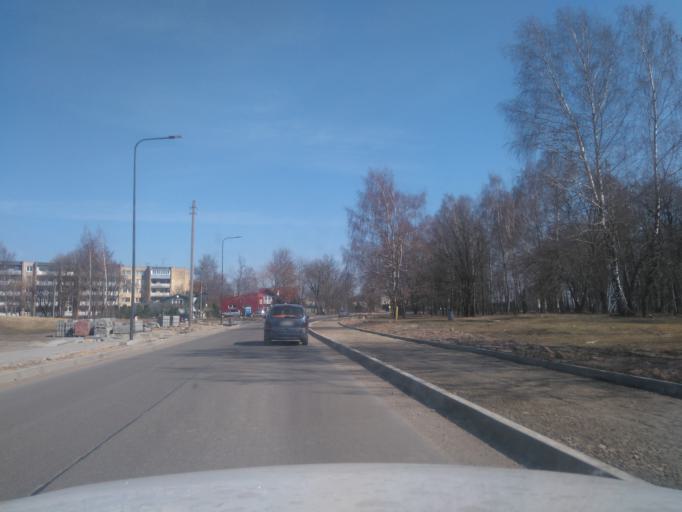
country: LT
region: Kauno apskritis
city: Dainava (Kaunas)
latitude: 54.8853
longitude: 23.9514
